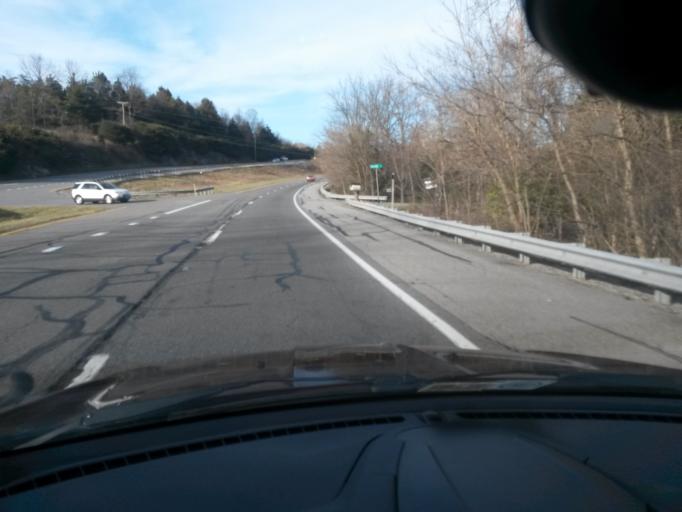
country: US
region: Virginia
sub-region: Botetourt County
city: Fincastle
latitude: 37.4700
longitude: -79.8820
